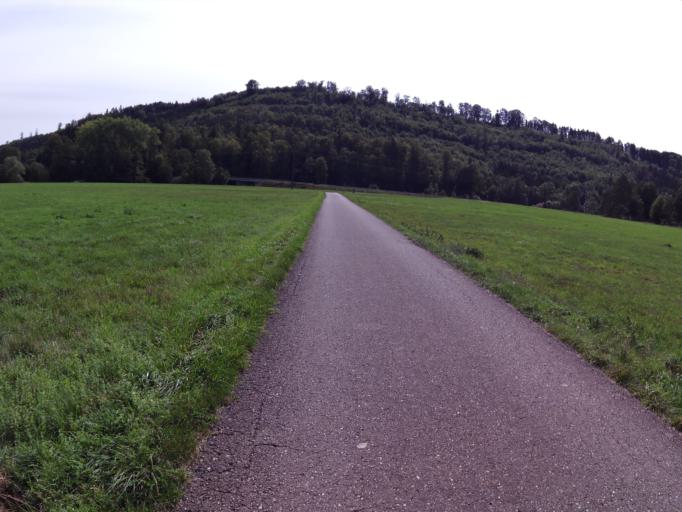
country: DE
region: Baden-Wuerttemberg
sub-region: Freiburg Region
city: Sulz am Neckar
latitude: 48.3972
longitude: 8.6427
